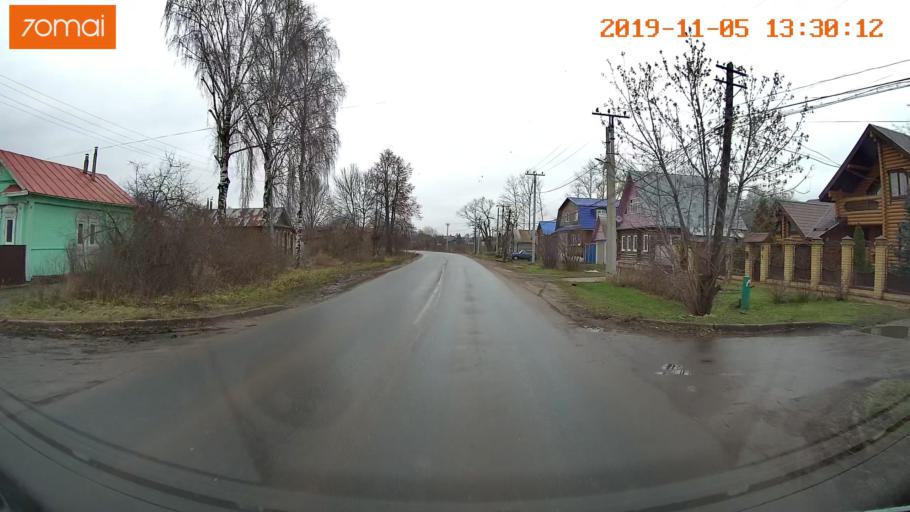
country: RU
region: Ivanovo
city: Shuya
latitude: 56.8653
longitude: 41.3969
